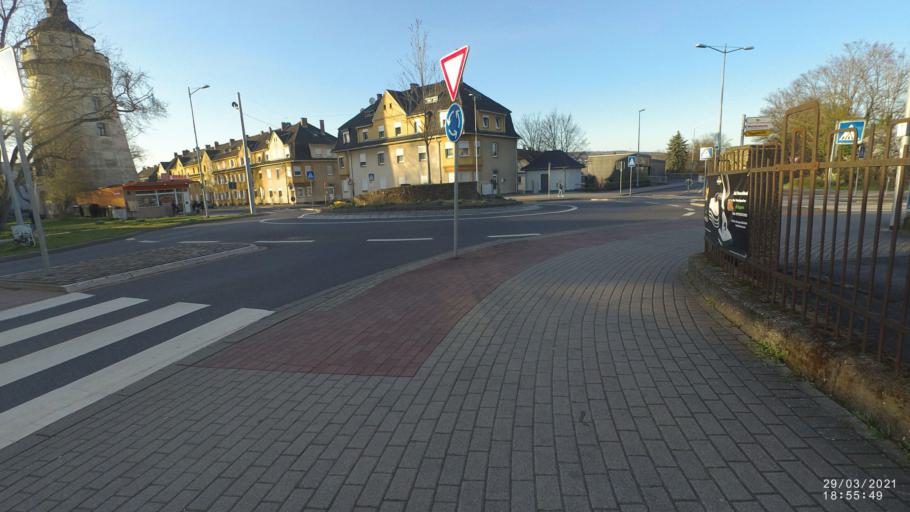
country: DE
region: Rheinland-Pfalz
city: Andernach
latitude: 50.4318
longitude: 7.4084
